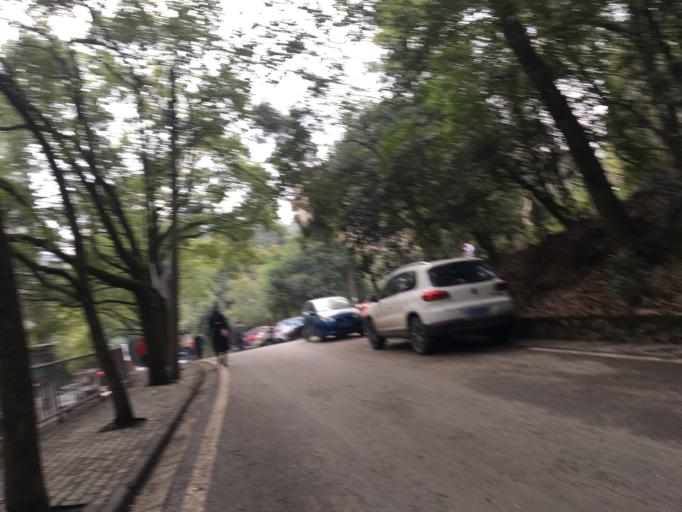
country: CN
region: Hubei
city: Guanshan
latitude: 30.5353
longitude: 114.3665
